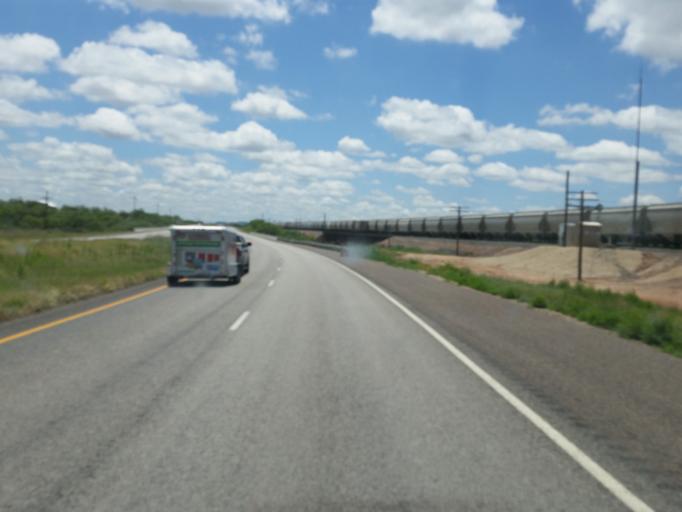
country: US
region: Texas
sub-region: Garza County
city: Post
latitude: 33.0404
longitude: -101.2009
